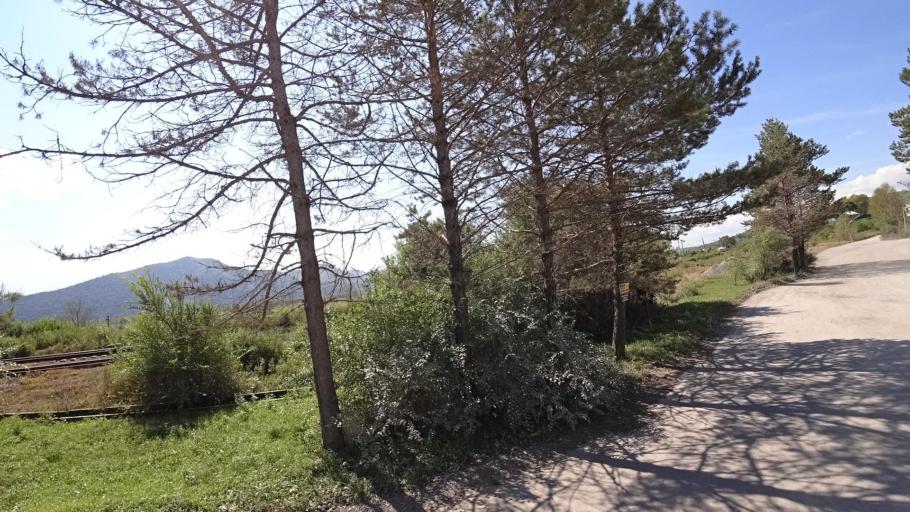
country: RU
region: Jewish Autonomous Oblast
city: Londoko
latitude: 49.0021
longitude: 131.8876
